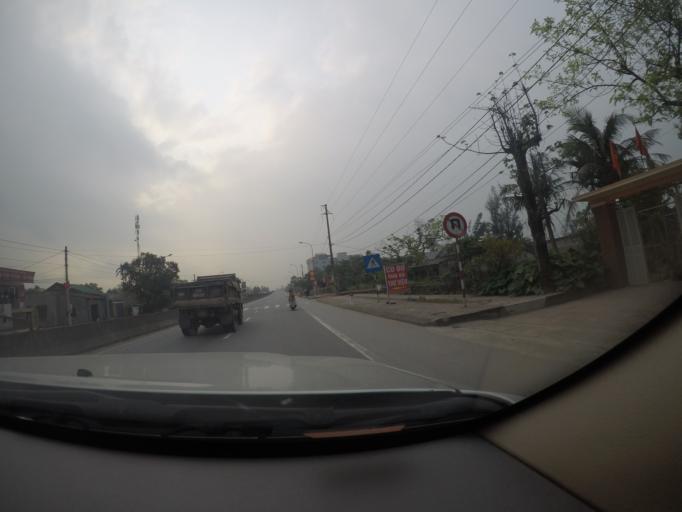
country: VN
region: Ha Tinh
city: Cam Xuyen
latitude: 18.2430
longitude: 106.0117
